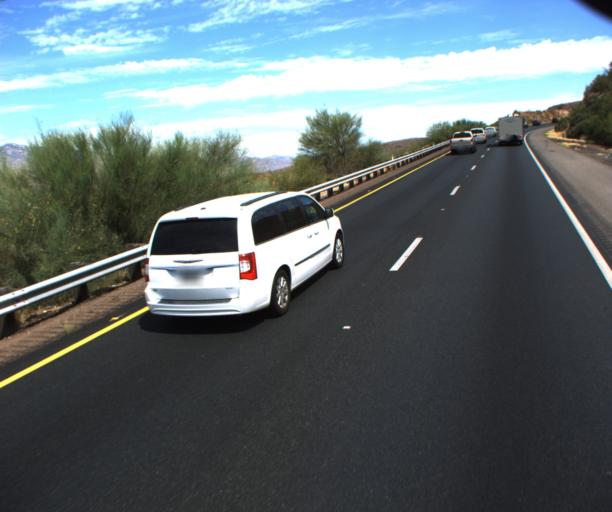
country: US
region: Arizona
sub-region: Yavapai County
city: Black Canyon City
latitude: 34.1482
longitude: -112.1411
